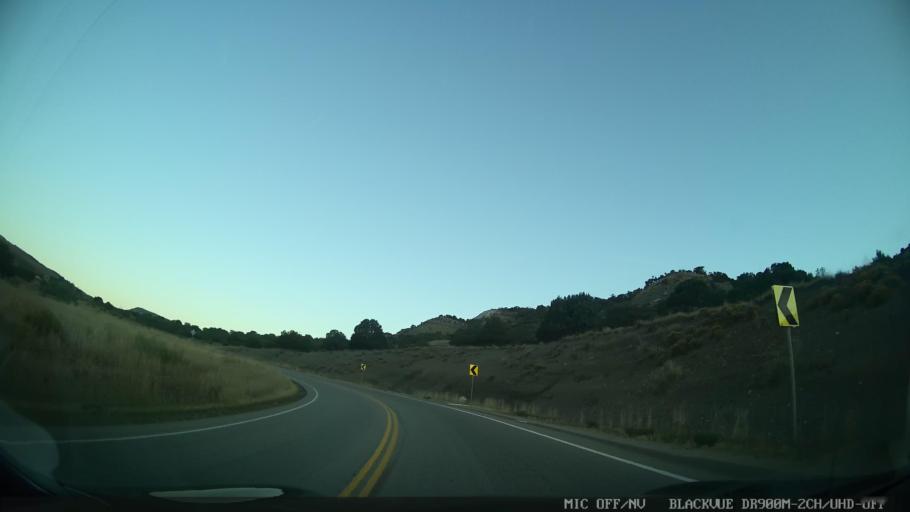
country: US
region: Colorado
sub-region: Eagle County
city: Edwards
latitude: 39.7037
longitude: -106.6776
